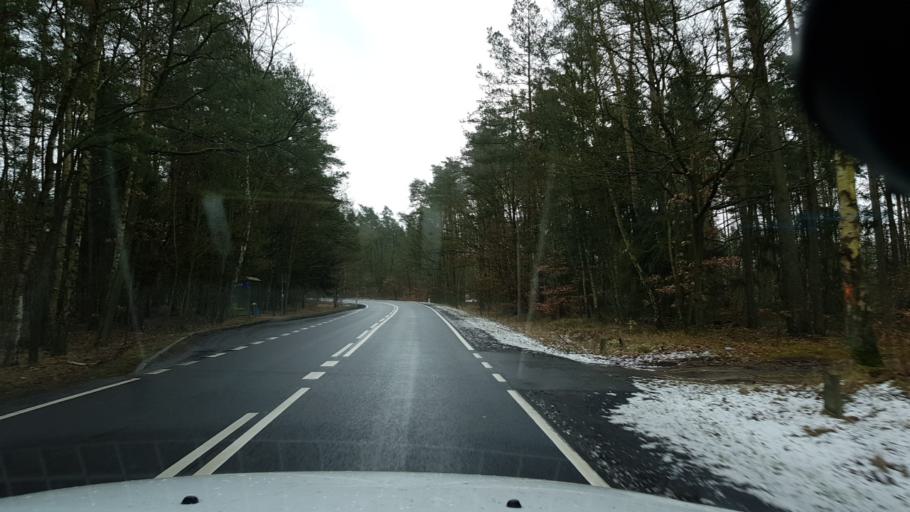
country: PL
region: West Pomeranian Voivodeship
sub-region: Powiat goleniowski
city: Stepnica
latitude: 53.6258
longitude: 14.6839
